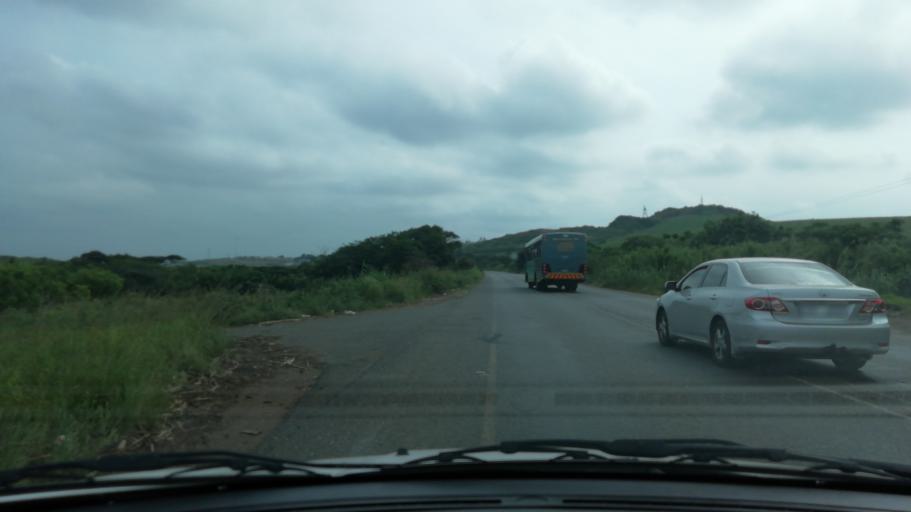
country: ZA
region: KwaZulu-Natal
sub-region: uThungulu District Municipality
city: Empangeni
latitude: -28.7501
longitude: 31.8789
